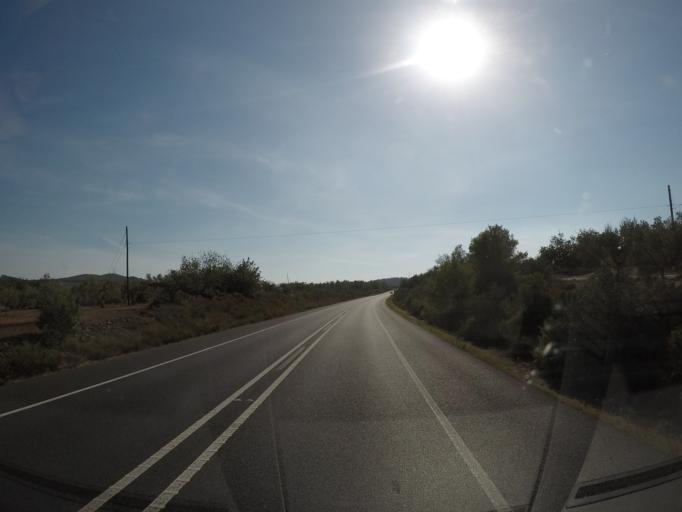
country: ES
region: Catalonia
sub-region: Provincia de Tarragona
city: El Perello
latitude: 40.8935
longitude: 0.7273
